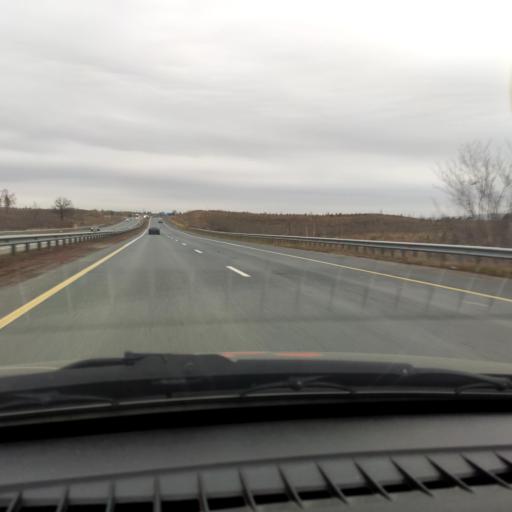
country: RU
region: Samara
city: Zhigulevsk
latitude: 53.5113
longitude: 49.5377
